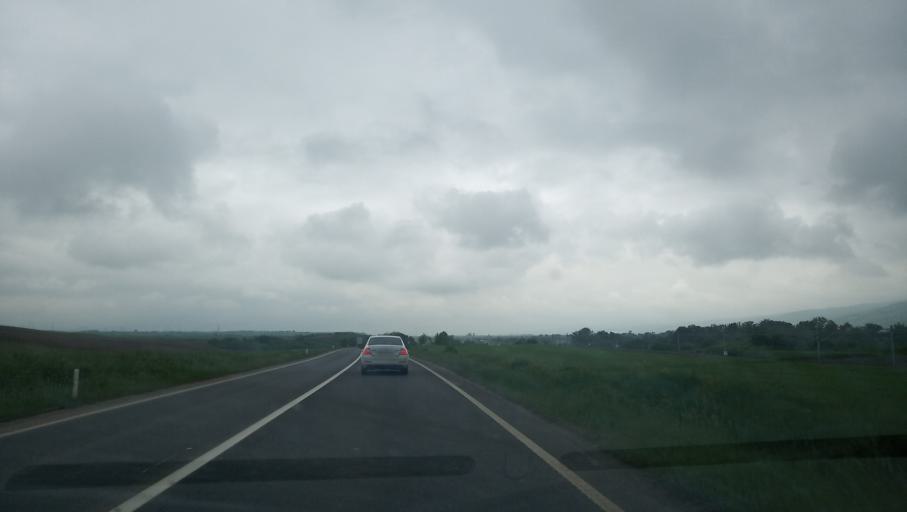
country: RO
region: Alba
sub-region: Comuna Blandiana
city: Blandiana
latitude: 45.9461
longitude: 23.4049
